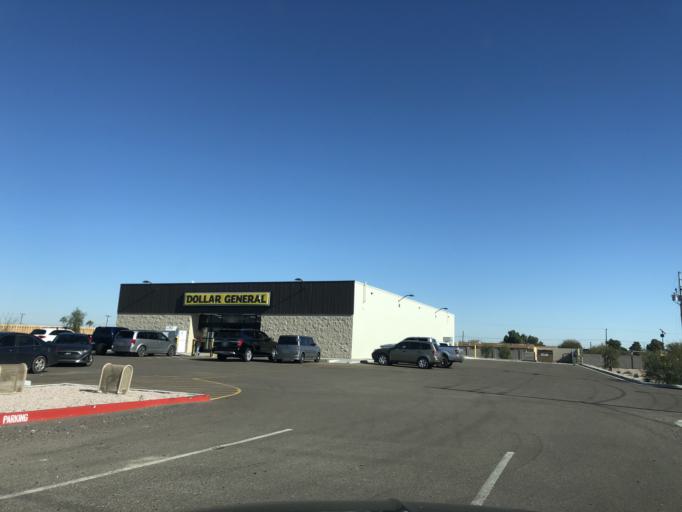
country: US
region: Arizona
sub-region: Maricopa County
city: Citrus Park
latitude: 33.4668
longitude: -112.4788
